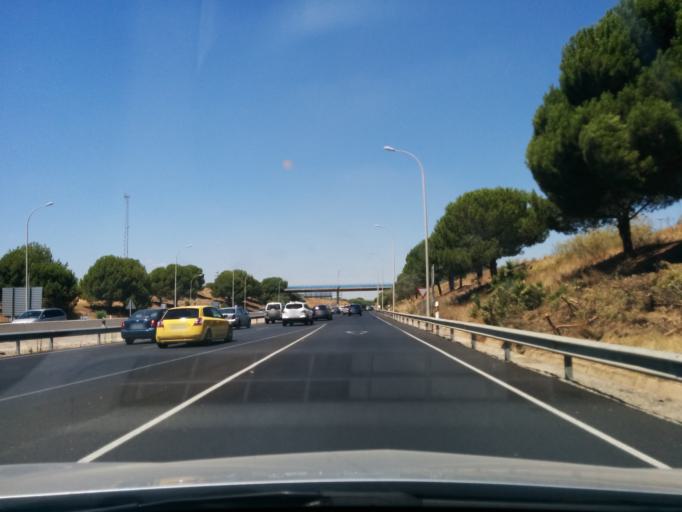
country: ES
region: Andalusia
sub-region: Provincia de Sevilla
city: Benacazon
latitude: 37.3614
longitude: -6.2004
